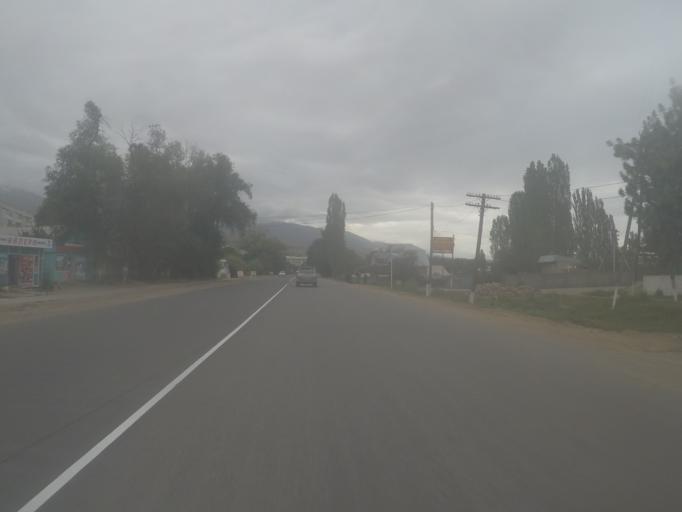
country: KG
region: Ysyk-Koel
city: Cholpon-Ata
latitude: 42.6721
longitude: 77.2951
